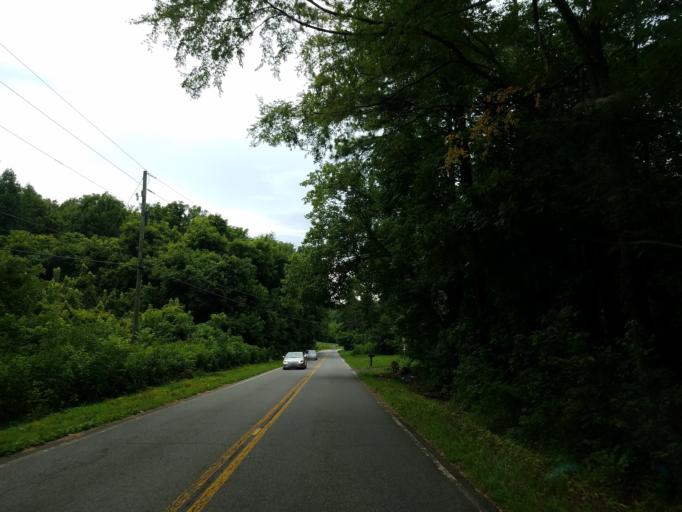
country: US
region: Georgia
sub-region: Bartow County
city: Cartersville
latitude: 34.2576
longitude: -84.8582
